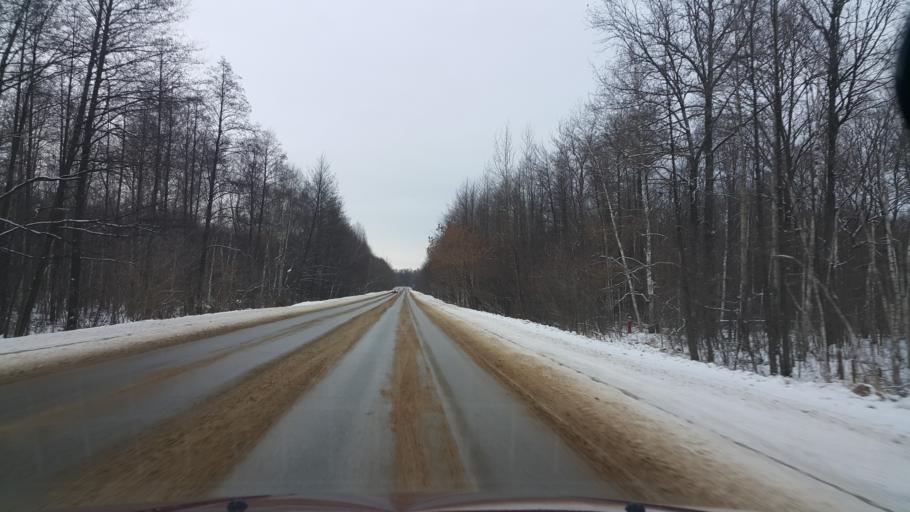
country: RU
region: Tambov
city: Kotovsk
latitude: 52.6240
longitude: 41.5142
